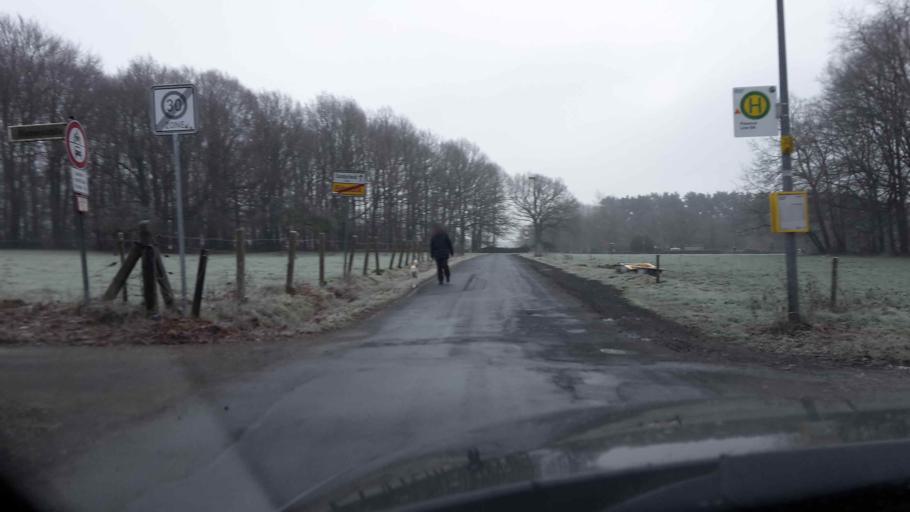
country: DE
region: North Rhine-Westphalia
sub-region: Regierungsbezirk Koln
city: Hennef
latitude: 50.7143
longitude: 7.3026
